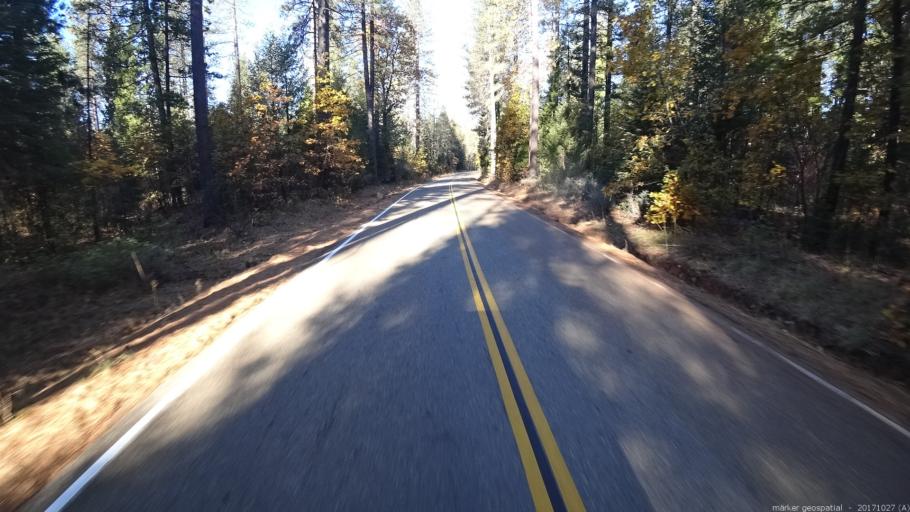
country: US
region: California
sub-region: Shasta County
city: Burney
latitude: 40.9312
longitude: -121.9435
